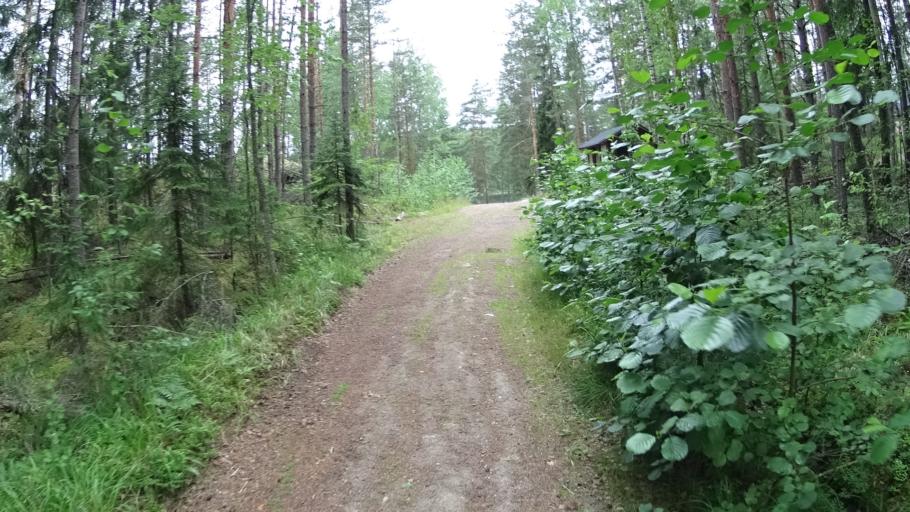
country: FI
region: Southern Savonia
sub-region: Mikkeli
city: Maentyharju
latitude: 61.1842
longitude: 26.8260
